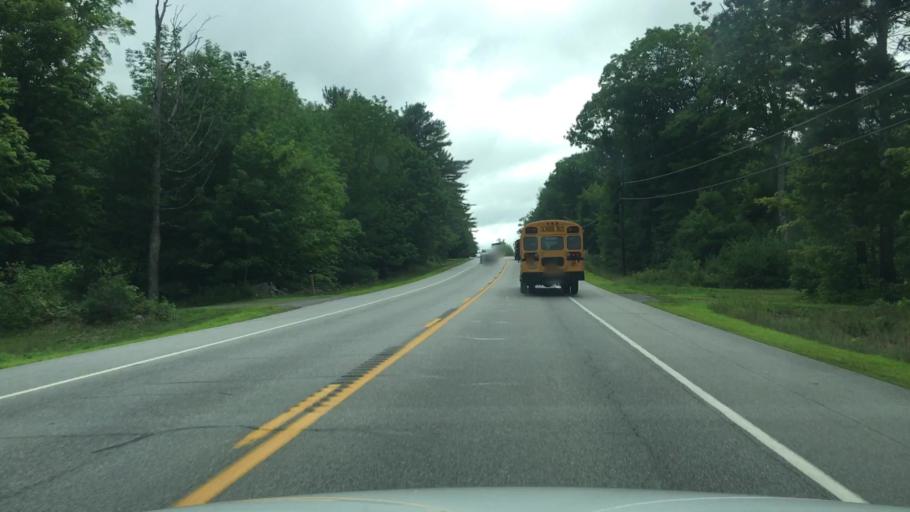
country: US
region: Maine
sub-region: Kennebec County
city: Windsor
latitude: 44.2782
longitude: -69.6205
